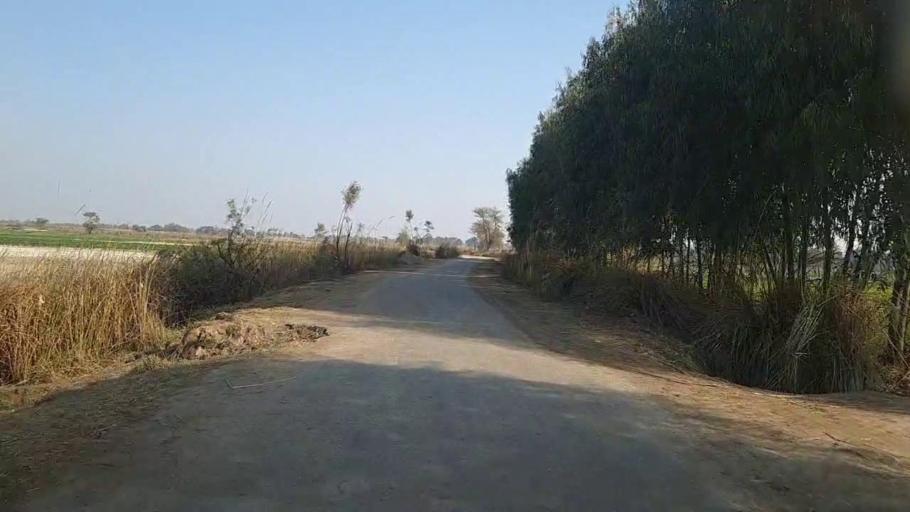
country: PK
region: Sindh
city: Mirpur Mathelo
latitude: 27.8749
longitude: 69.6261
